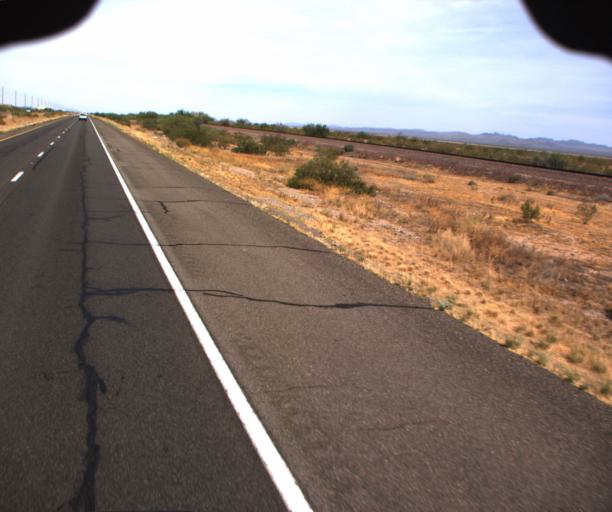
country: US
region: Arizona
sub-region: Maricopa County
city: Sun City West
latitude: 33.7285
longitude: -112.4651
